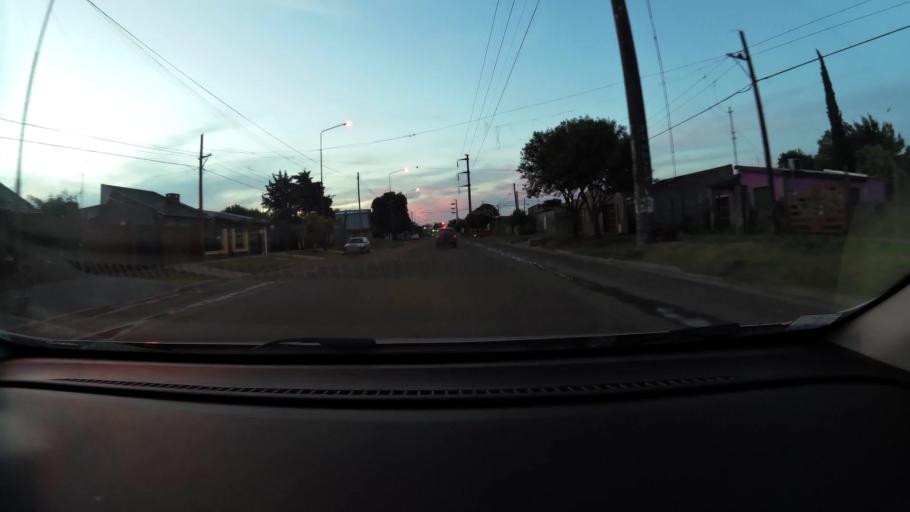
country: AR
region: Buenos Aires
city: San Nicolas de los Arroyos
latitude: -33.3531
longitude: -60.2126
